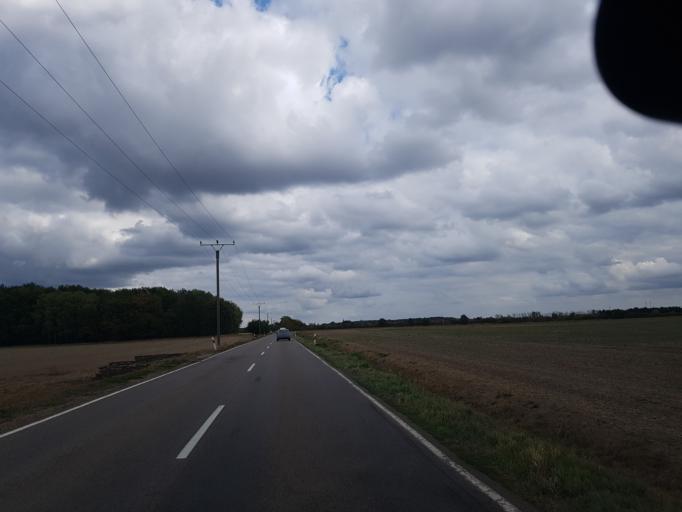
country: DE
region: Saxony-Anhalt
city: Klieken
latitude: 51.9298
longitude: 12.3636
